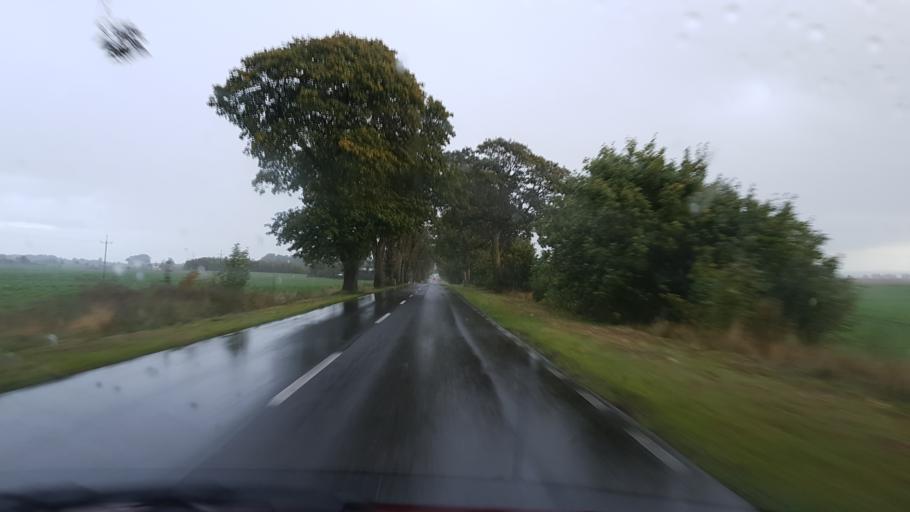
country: PL
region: Greater Poland Voivodeship
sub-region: Powiat pilski
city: Szydlowo
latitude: 53.1709
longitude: 16.5794
